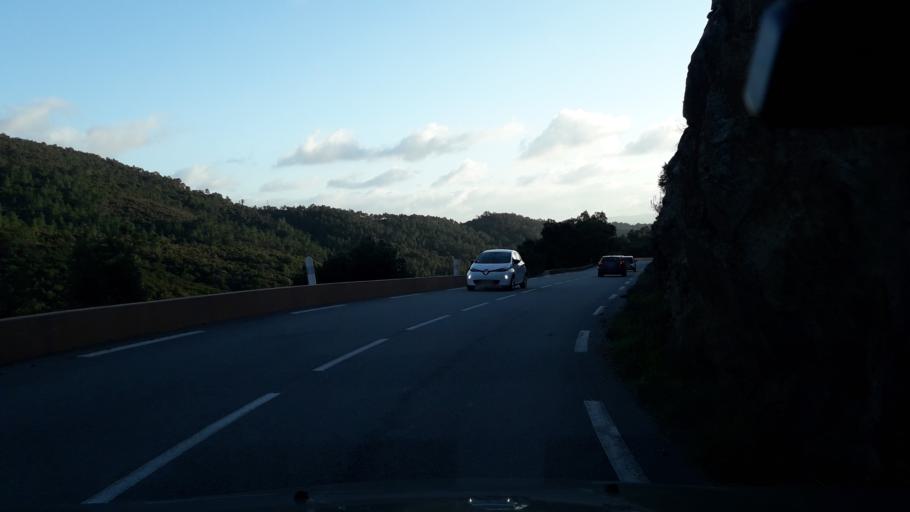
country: FR
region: Provence-Alpes-Cote d'Azur
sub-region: Departement du Var
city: Saint-Raphael
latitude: 43.4840
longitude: 6.7784
